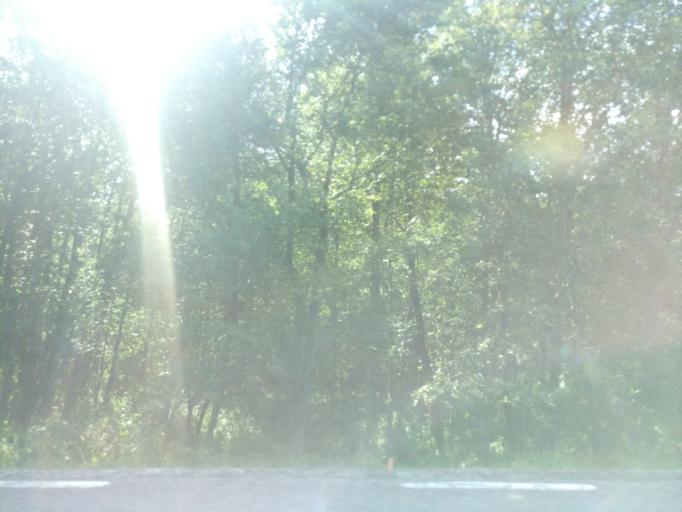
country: SE
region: Vaermland
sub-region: Hagfors Kommun
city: Ekshaerad
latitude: 60.3619
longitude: 13.3141
